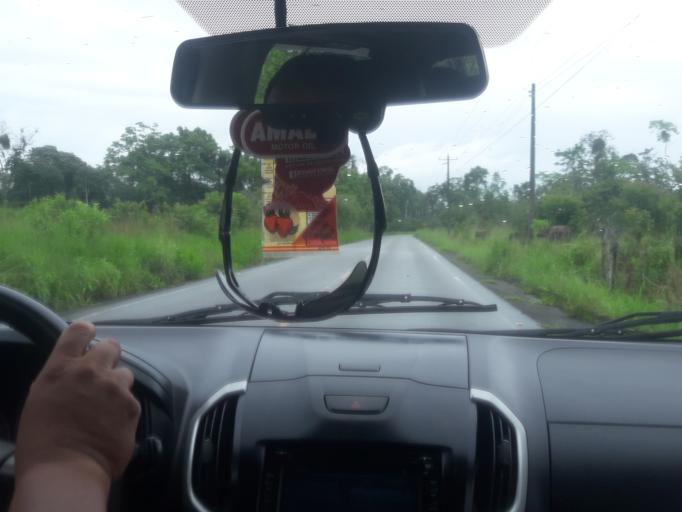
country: EC
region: Napo
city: Tena
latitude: -1.0340
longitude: -77.6784
